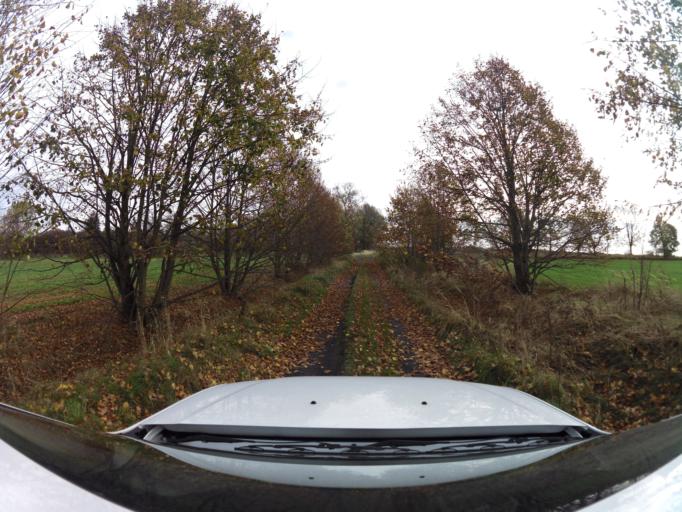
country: PL
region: West Pomeranian Voivodeship
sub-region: Powiat gryficki
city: Cerkwica
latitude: 54.0503
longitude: 15.0992
